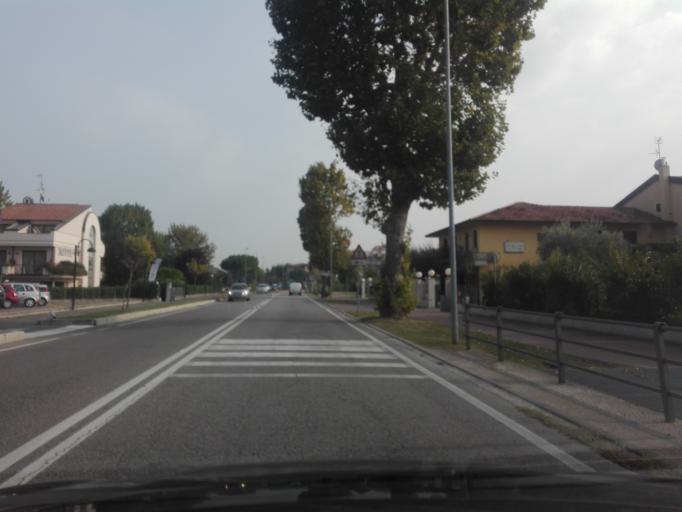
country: IT
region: Lombardy
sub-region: Provincia di Brescia
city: San Martino della Battaglia
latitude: 45.4638
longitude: 10.6146
